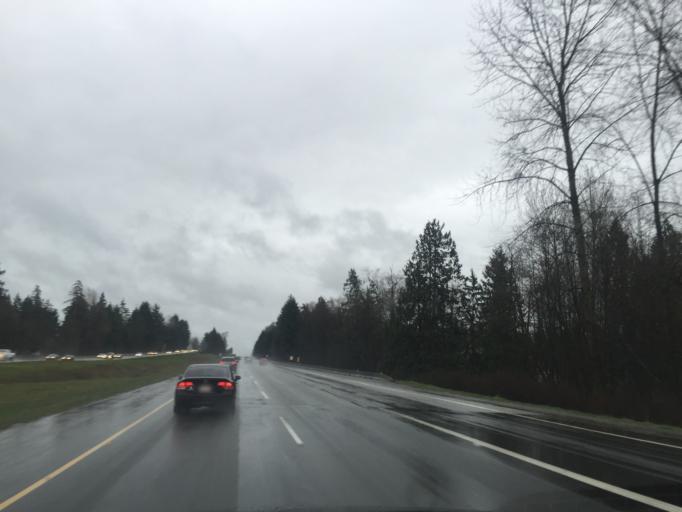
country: CA
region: British Columbia
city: Langley
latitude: 49.1322
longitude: -122.5713
